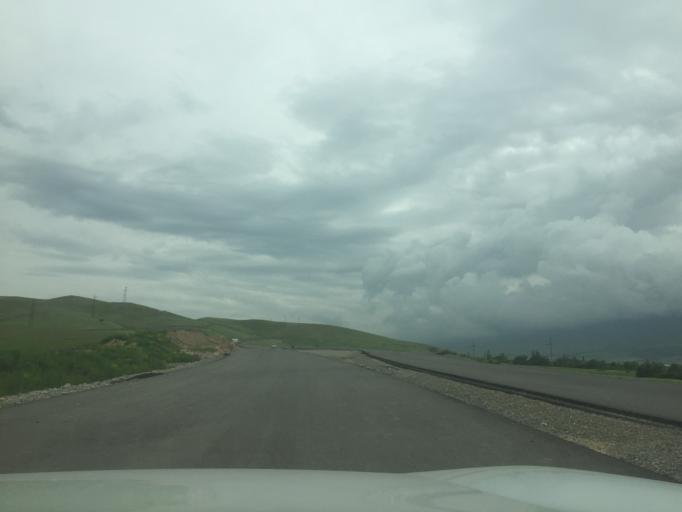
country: KZ
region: Ongtustik Qazaqstan
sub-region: Tulkibas Audany
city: Zhabagly
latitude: 42.5173
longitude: 70.5549
